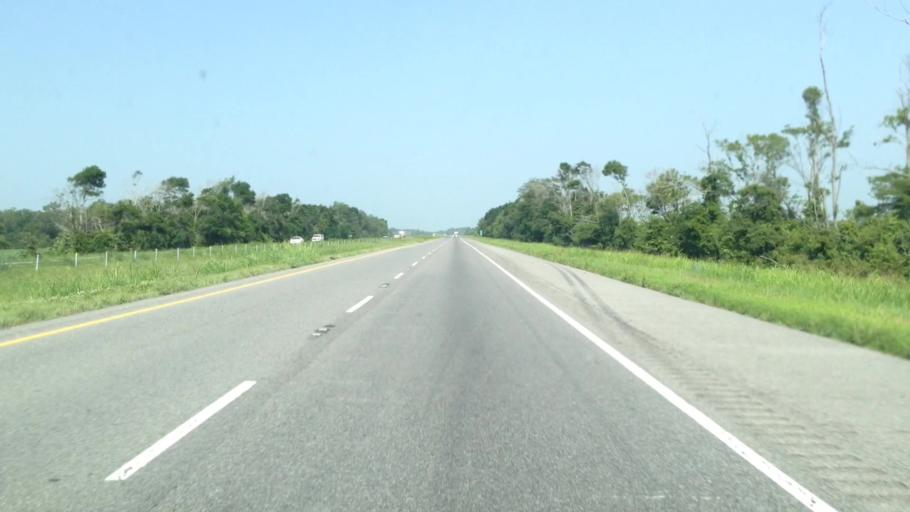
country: US
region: Louisiana
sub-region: Madison Parish
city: Tallulah
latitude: 32.4127
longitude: -91.2639
